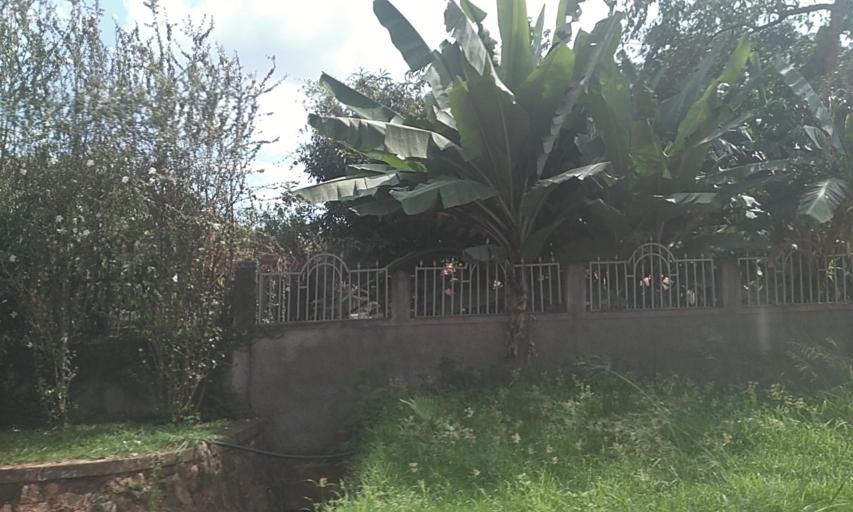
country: UG
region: Central Region
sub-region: Wakiso District
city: Kireka
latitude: 0.3443
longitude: 32.6141
